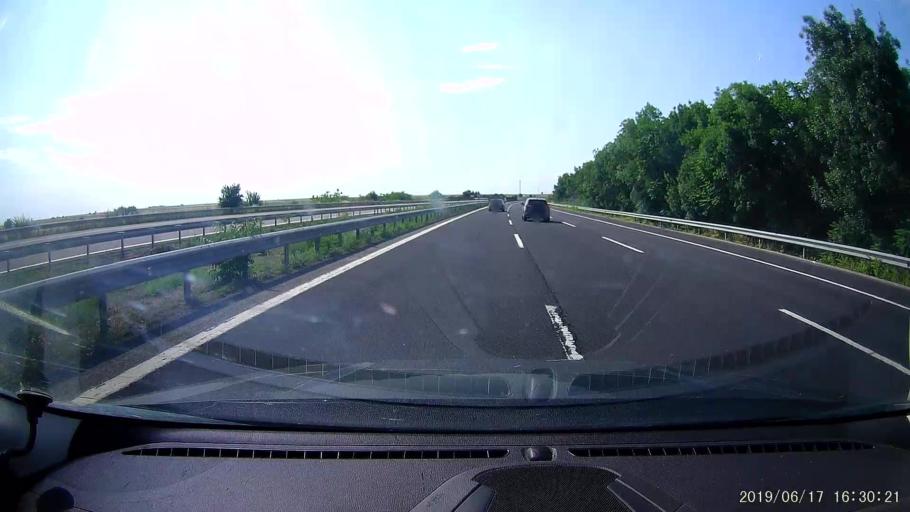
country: TR
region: Tekirdag
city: Beyazkoy
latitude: 41.3451
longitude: 27.6559
